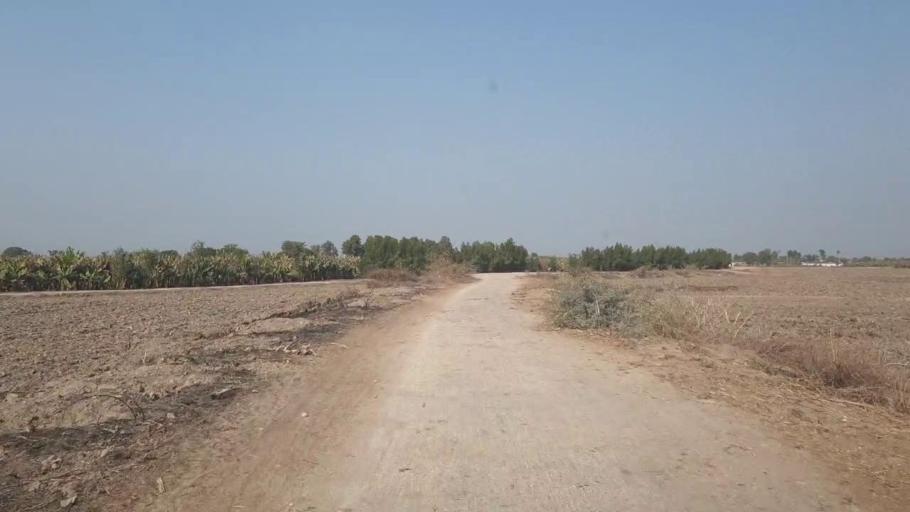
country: PK
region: Sindh
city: Tando Allahyar
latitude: 25.4454
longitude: 68.7868
